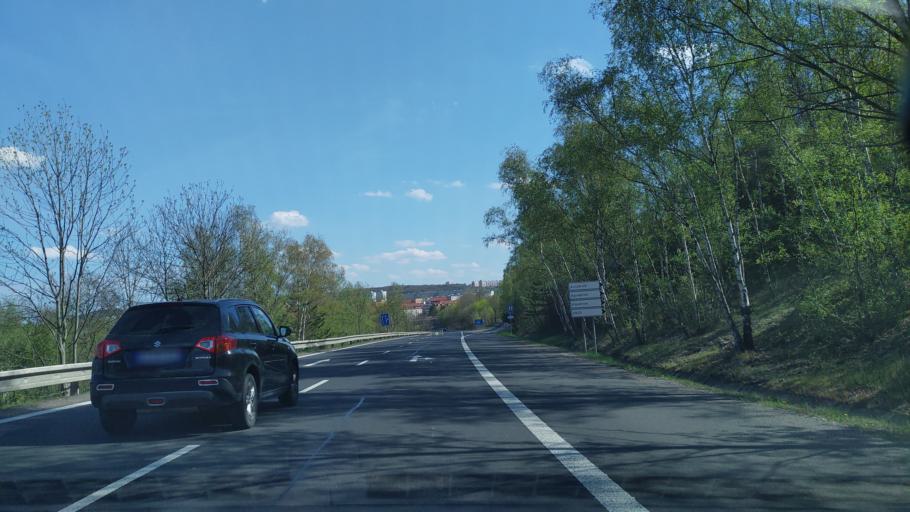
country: CZ
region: Ustecky
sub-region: Okres Most
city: Most
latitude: 50.5212
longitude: 13.6384
